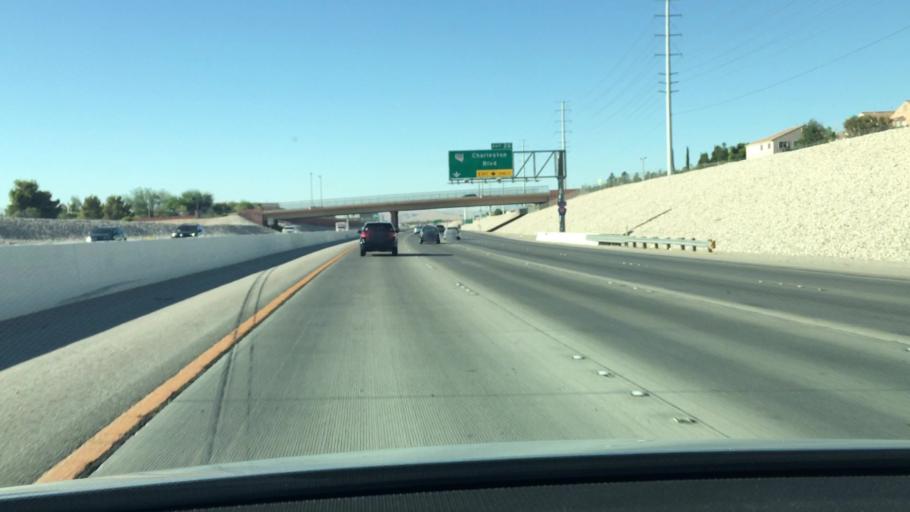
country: US
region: Nevada
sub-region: Clark County
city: Summerlin South
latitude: 36.1724
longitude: -115.3379
